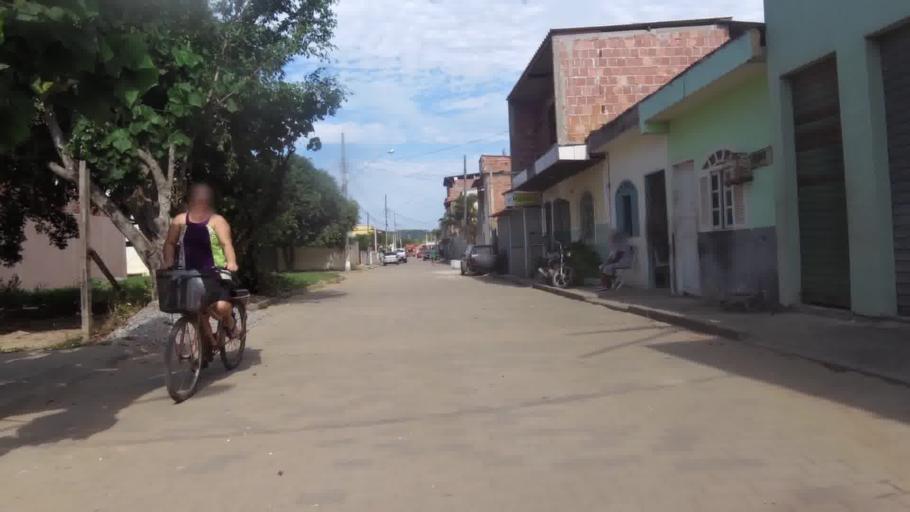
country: BR
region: Espirito Santo
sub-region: Piuma
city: Piuma
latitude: -20.8476
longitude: -40.7497
